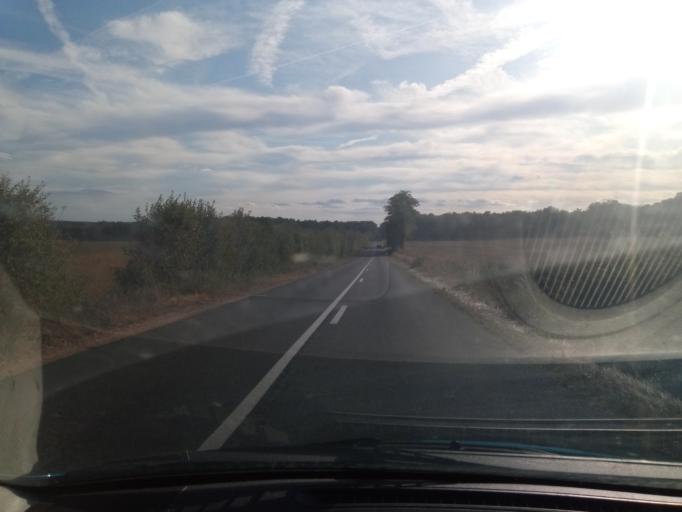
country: FR
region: Poitou-Charentes
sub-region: Departement de la Vienne
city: Saint-Savin
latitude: 46.5026
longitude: 0.8491
